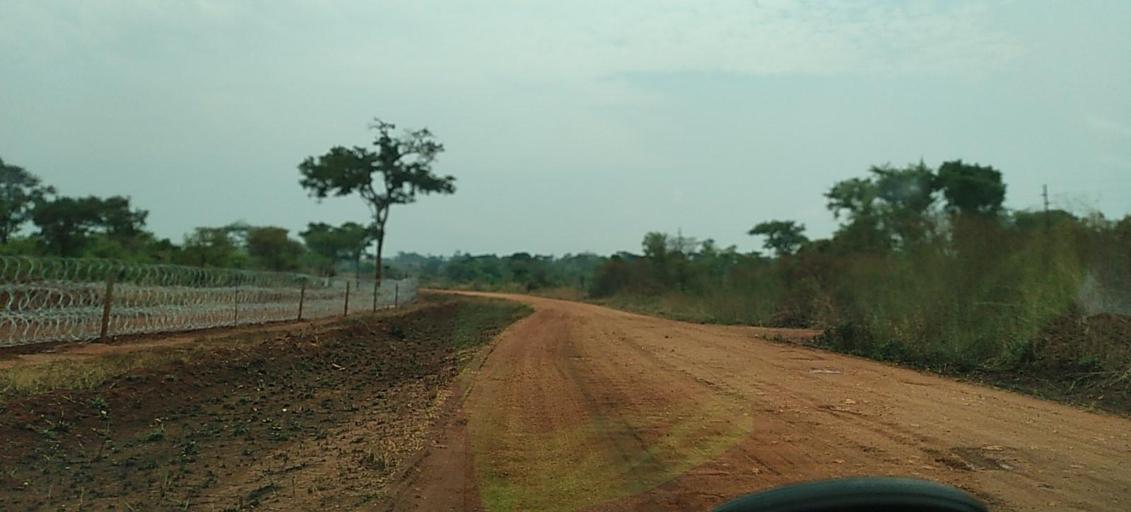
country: ZM
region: North-Western
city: Kansanshi
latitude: -12.1087
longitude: 26.4900
